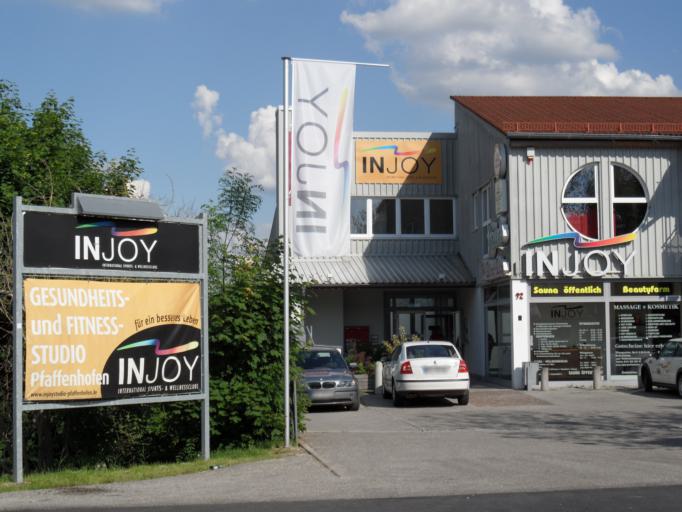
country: DE
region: Bavaria
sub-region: Upper Bavaria
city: Pfaffenhofen an der Ilm
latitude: 48.5425
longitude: 11.5091
